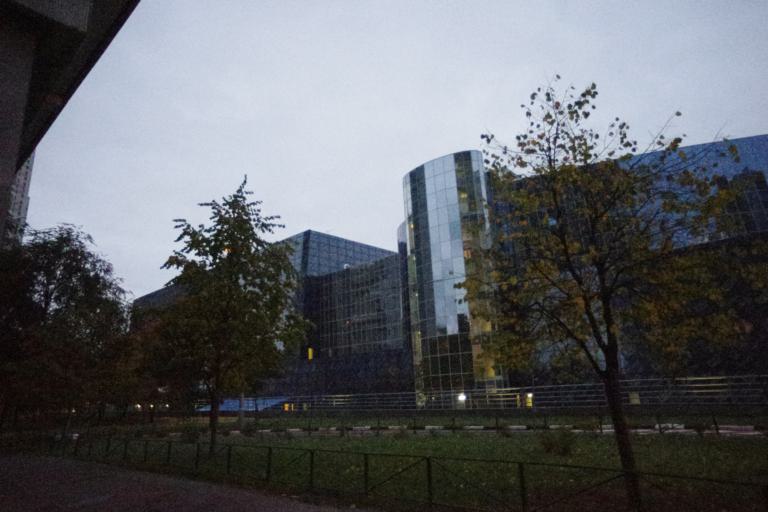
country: RU
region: Moscow
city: Troparevo
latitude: 55.6635
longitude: 37.5126
